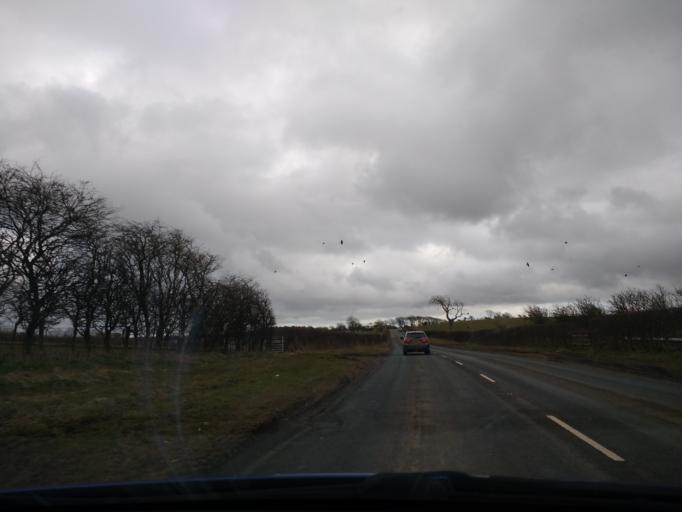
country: GB
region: England
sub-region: Cumbria
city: Dearham
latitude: 54.6914
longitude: -3.4094
